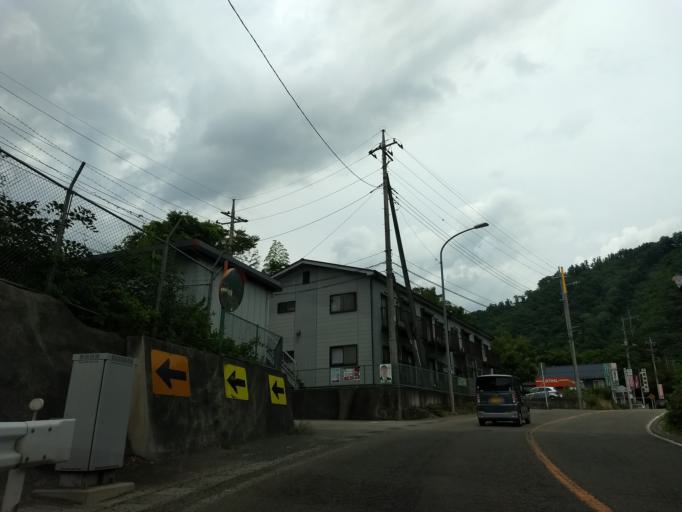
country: JP
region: Yamanashi
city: Otsuki
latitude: 35.5805
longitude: 138.9357
